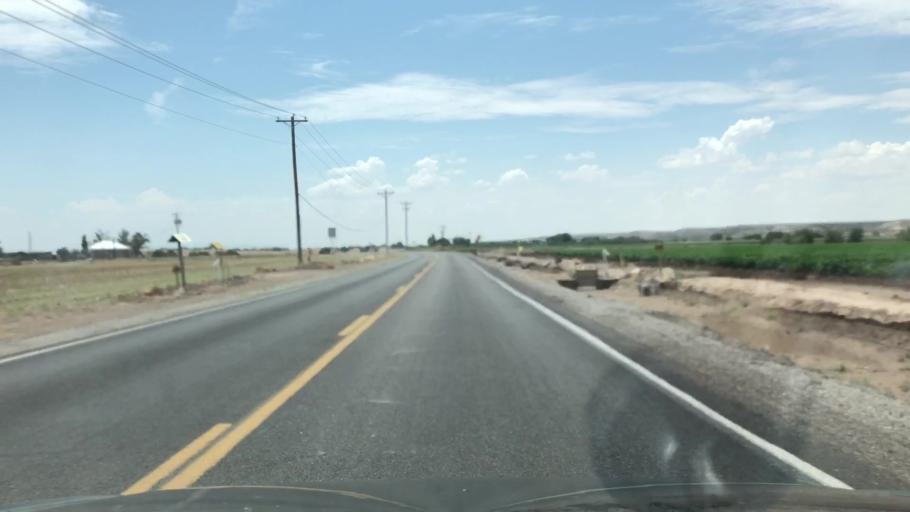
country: US
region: New Mexico
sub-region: Dona Ana County
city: Vado
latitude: 32.0735
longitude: -106.6835
